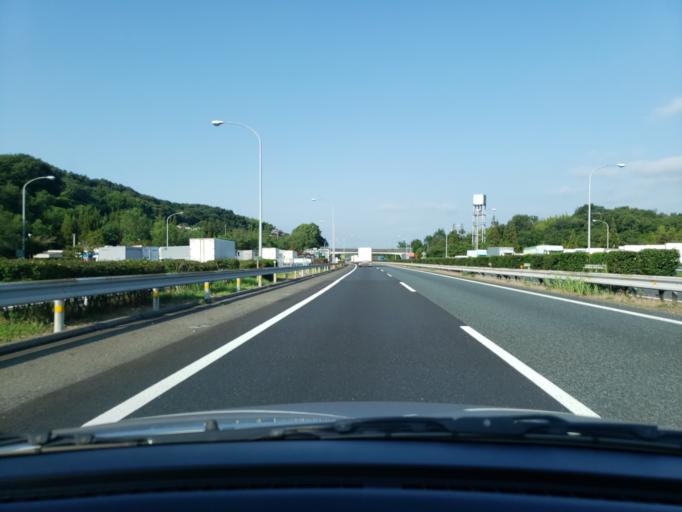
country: JP
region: Hiroshima
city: Kannabecho-yahiro
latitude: 34.5365
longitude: 133.4587
